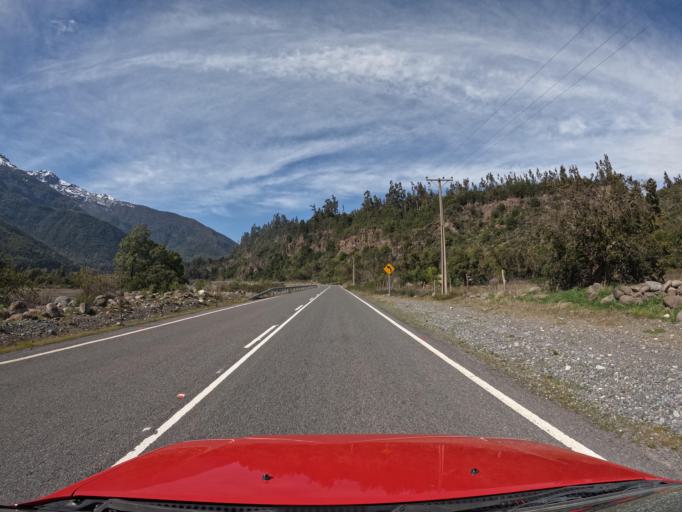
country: CL
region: Maule
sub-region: Provincia de Curico
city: Teno
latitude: -35.0039
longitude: -70.8292
